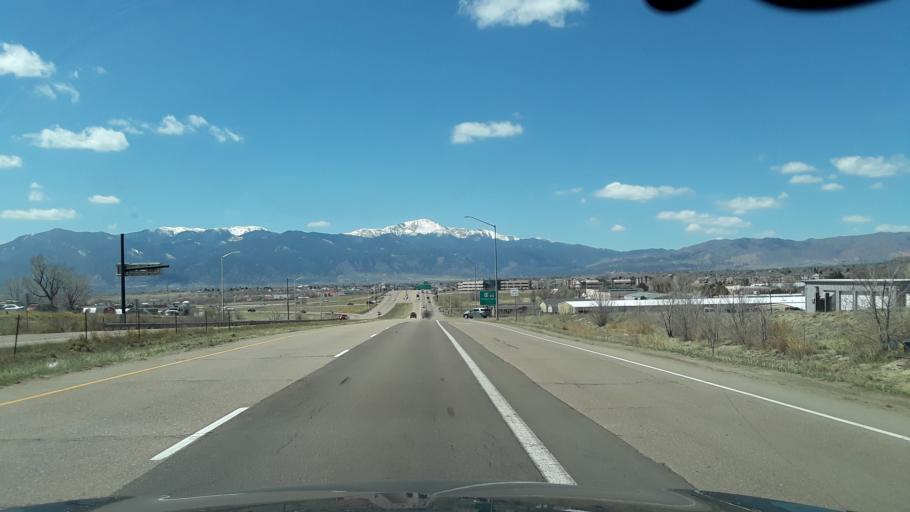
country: US
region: Colorado
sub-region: El Paso County
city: Cimarron Hills
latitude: 38.8391
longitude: -104.7126
